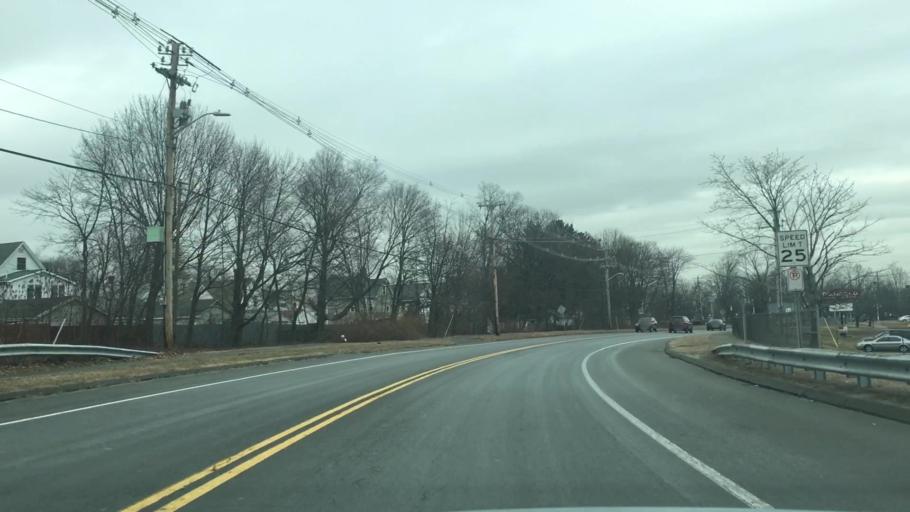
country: US
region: Massachusetts
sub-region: Hampden County
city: Holyoke
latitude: 42.1883
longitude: -72.6327
